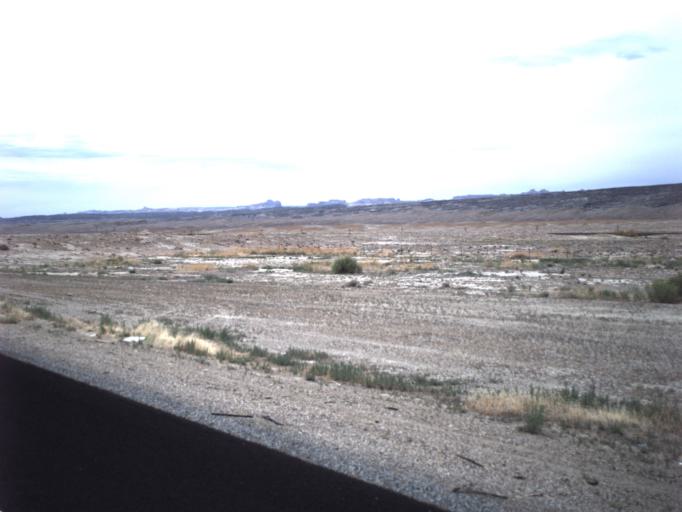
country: US
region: Utah
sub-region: Carbon County
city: East Carbon City
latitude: 39.1688
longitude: -110.3383
